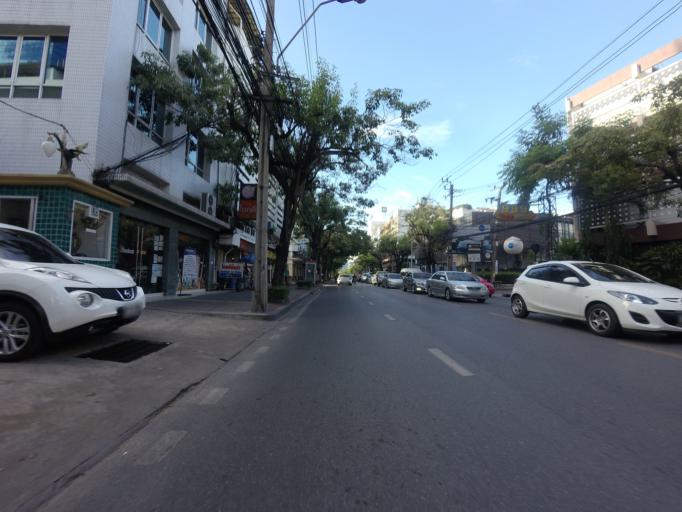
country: TH
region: Bangkok
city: Watthana
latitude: 13.7249
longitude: 100.5847
